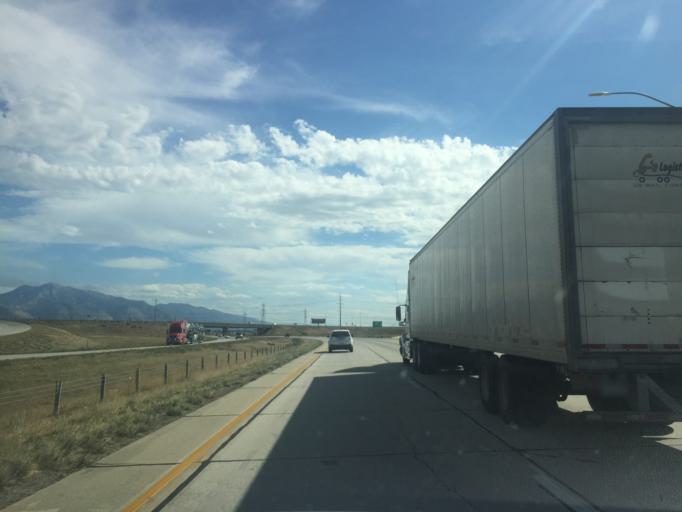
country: US
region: Utah
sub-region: Box Elder County
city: South Willard
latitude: 41.3445
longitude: -112.0391
